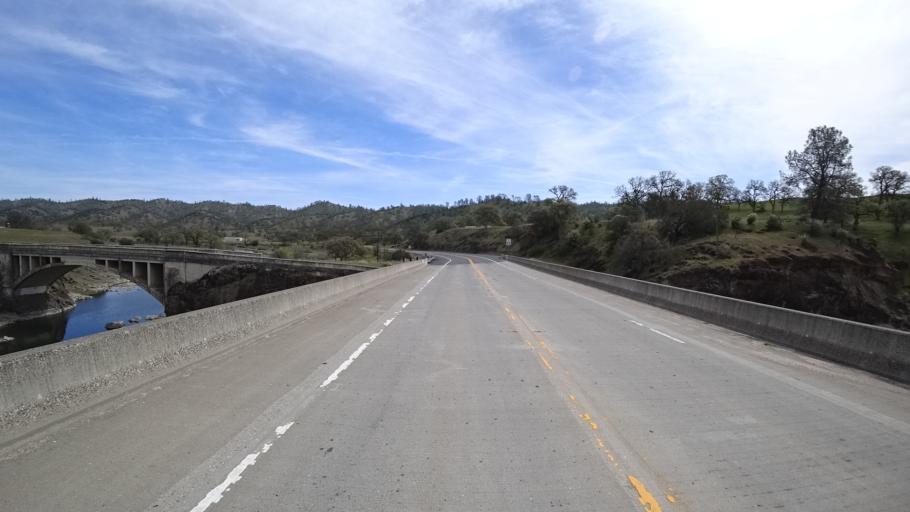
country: US
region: California
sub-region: Glenn County
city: Willows
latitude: 39.6114
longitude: -122.5292
